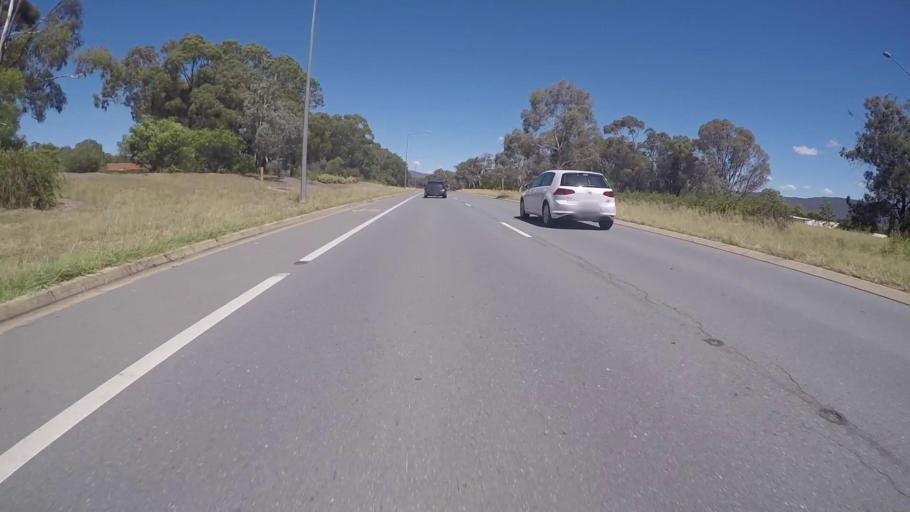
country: AU
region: Australian Capital Territory
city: Macarthur
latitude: -35.4062
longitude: 149.0741
